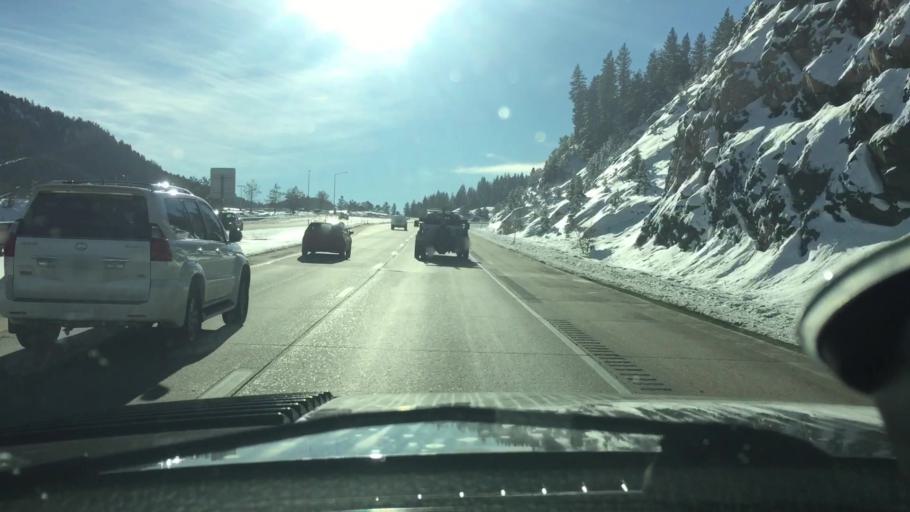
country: US
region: Colorado
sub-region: Jefferson County
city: Indian Hills
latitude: 39.6081
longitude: -105.2314
